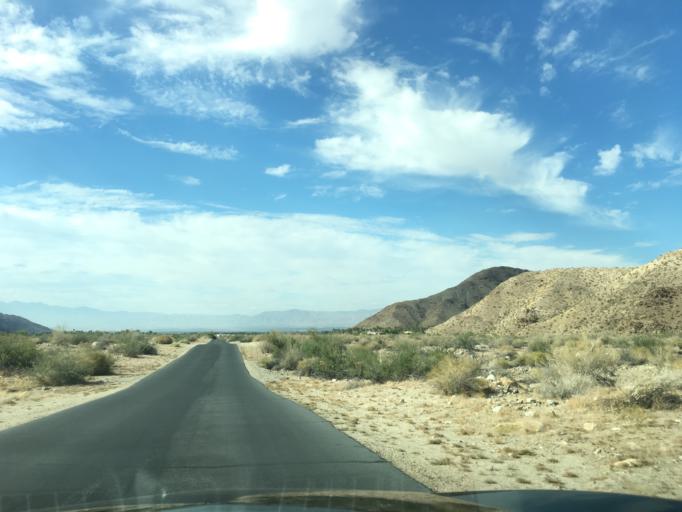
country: US
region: California
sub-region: Riverside County
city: Palm Springs
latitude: 33.7581
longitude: -116.5363
